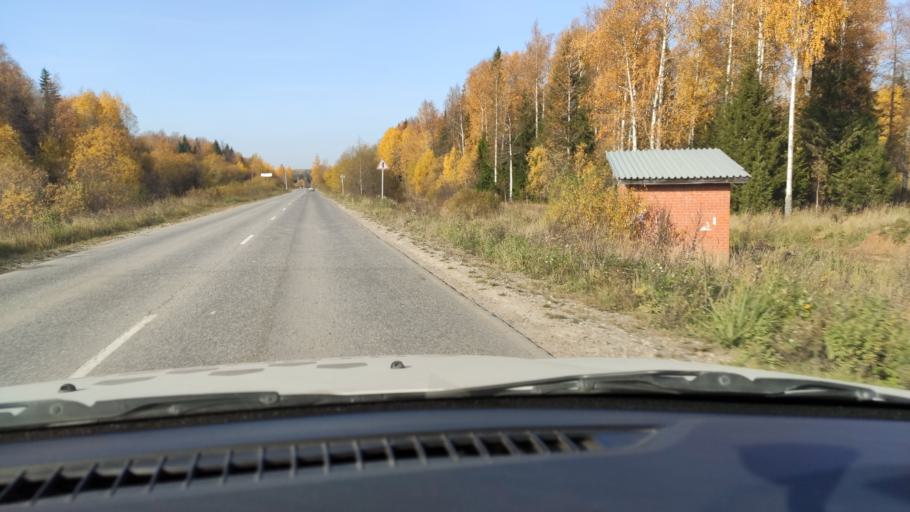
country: RU
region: Perm
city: Novyye Lyady
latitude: 58.0340
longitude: 56.6089
